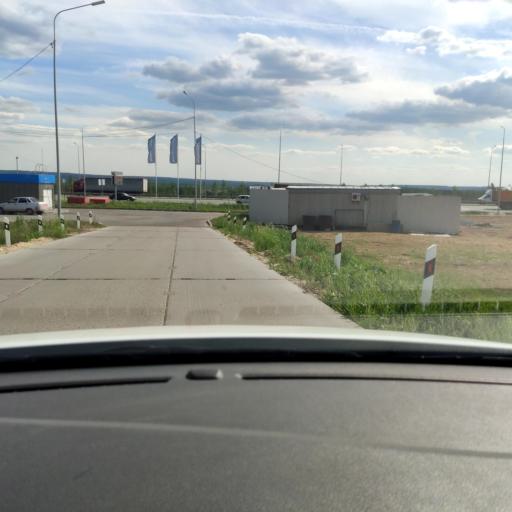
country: RU
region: Tatarstan
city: Pestretsy
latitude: 55.7120
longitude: 49.5491
